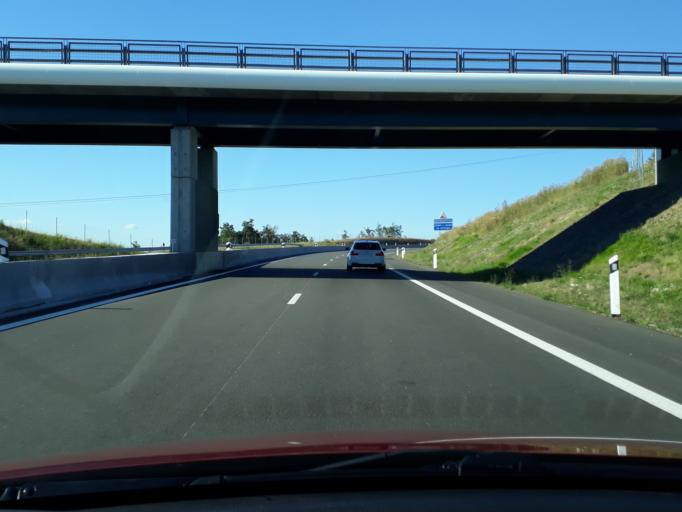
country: FR
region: Auvergne
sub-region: Departement de la Haute-Loire
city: Cussac-sur-Loire
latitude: 45.0081
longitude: 3.8833
